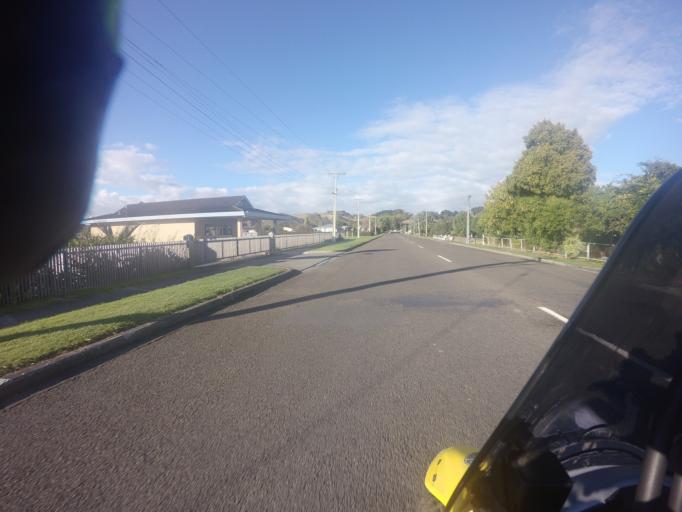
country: NZ
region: Gisborne
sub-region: Gisborne District
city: Gisborne
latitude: -38.6744
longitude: 178.0499
